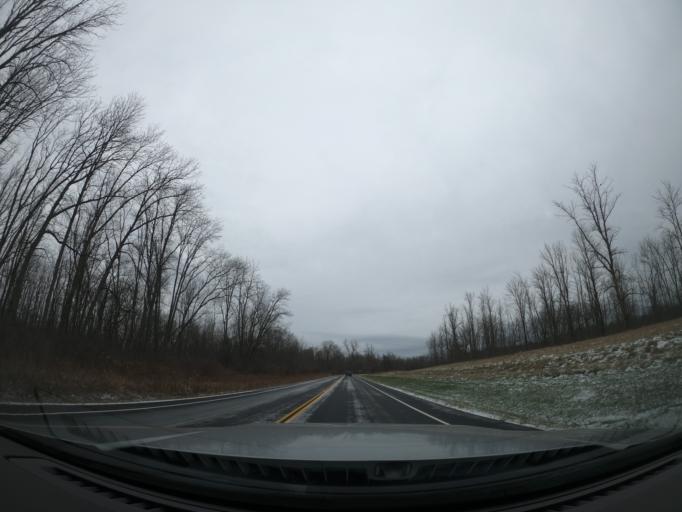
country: US
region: New York
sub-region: Tompkins County
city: Northeast Ithaca
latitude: 42.4850
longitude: -76.4567
